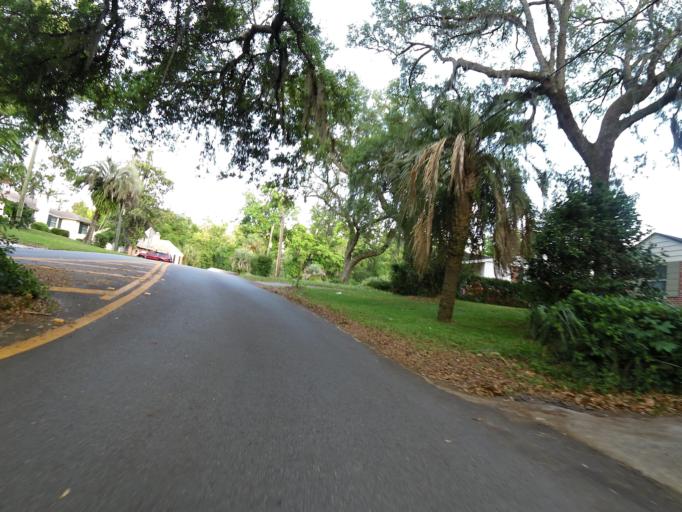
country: US
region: Florida
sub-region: Duval County
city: Jacksonville
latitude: 30.3057
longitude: -81.6277
